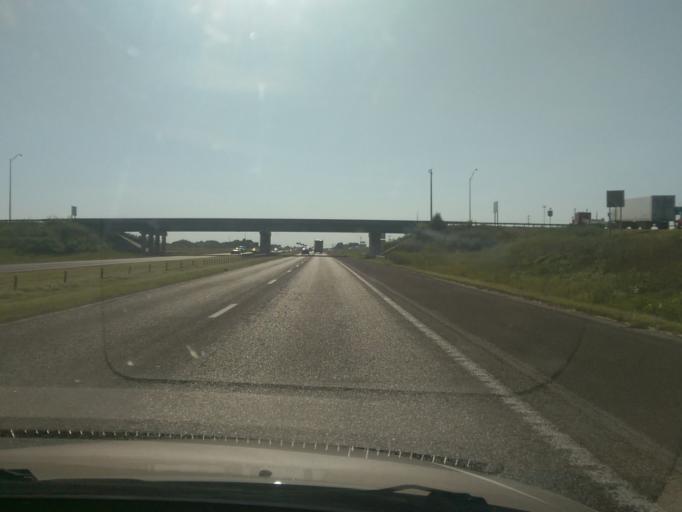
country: US
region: Missouri
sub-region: Lafayette County
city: Higginsville
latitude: 39.0009
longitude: -93.7338
